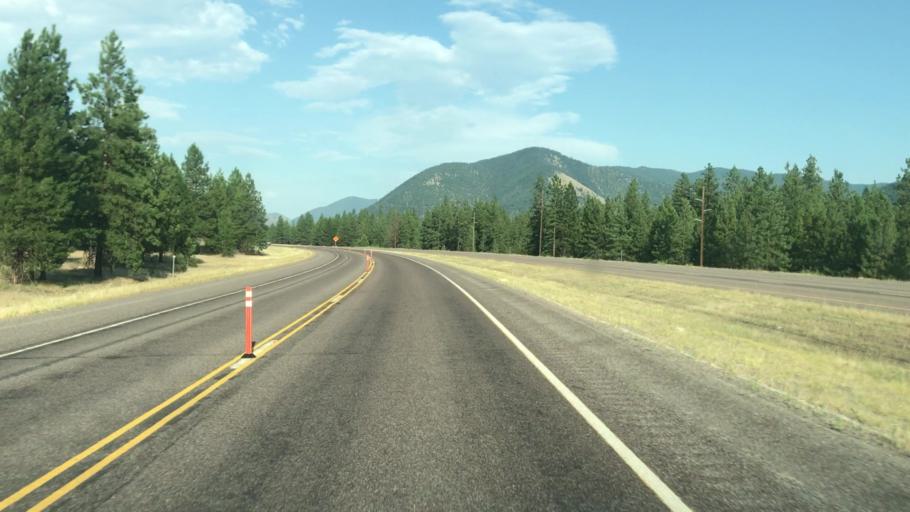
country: US
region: Montana
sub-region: Mineral County
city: Superior
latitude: 47.0118
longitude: -114.7221
